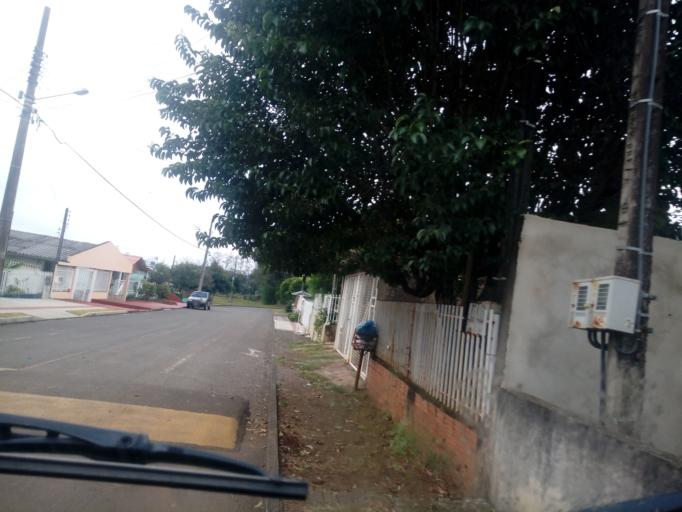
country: BR
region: Santa Catarina
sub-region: Chapeco
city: Chapeco
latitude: -27.1160
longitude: -52.6272
